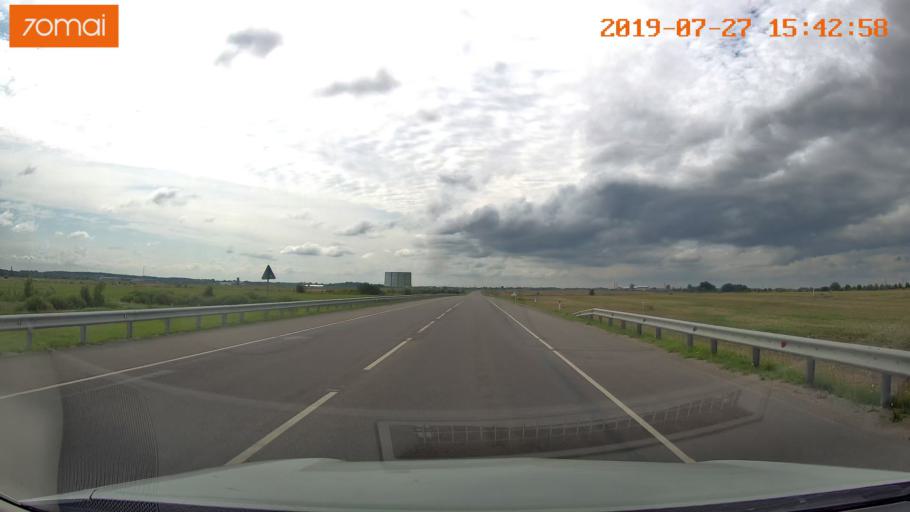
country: RU
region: Kaliningrad
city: Gusev
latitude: 54.6165
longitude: 22.2047
